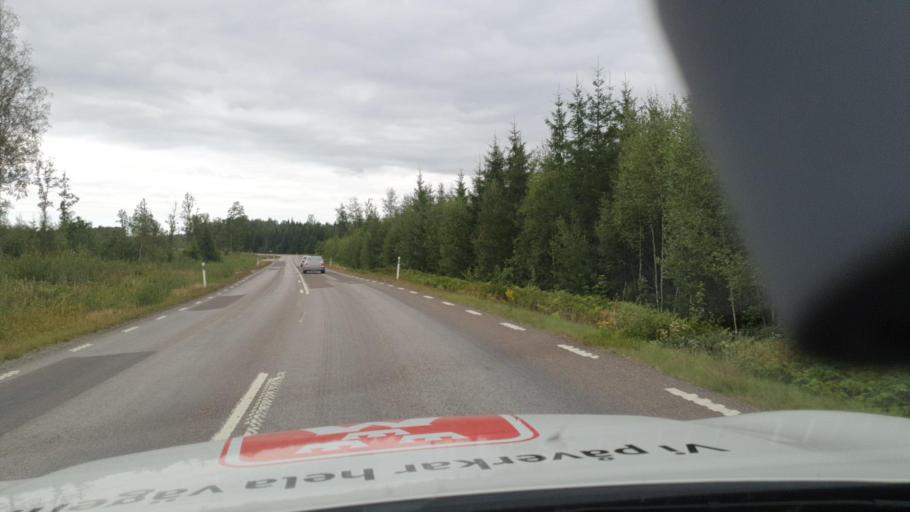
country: SE
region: Vaestra Goetaland
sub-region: Melleruds Kommun
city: Mellerud
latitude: 58.7150
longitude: 12.4111
